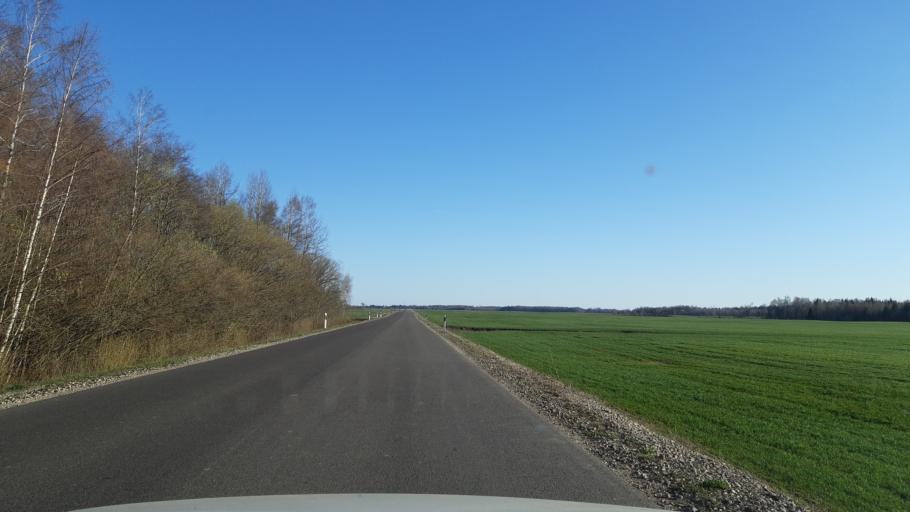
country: LT
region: Kauno apskritis
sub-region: Kaunas
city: Sargenai
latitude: 55.0290
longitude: 23.7600
